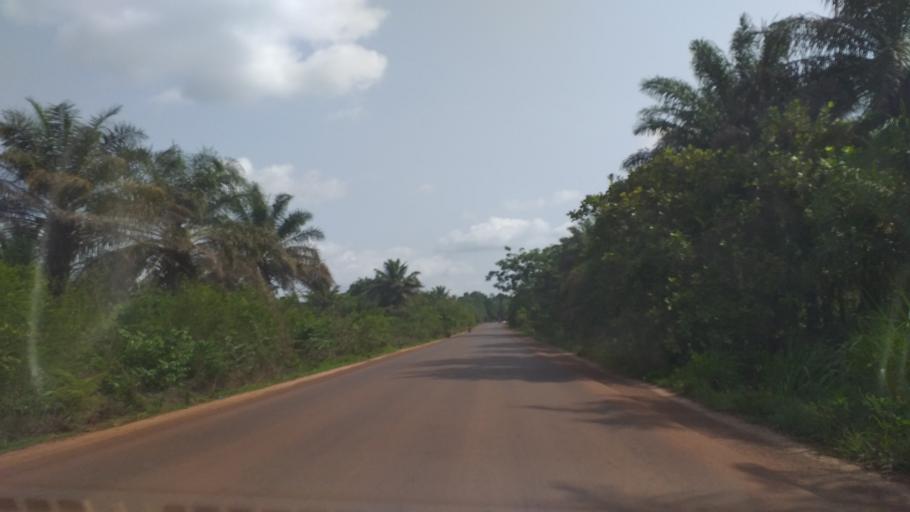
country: GN
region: Boke
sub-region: Boke Prefecture
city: Sangueya
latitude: 10.8248
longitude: -14.3715
